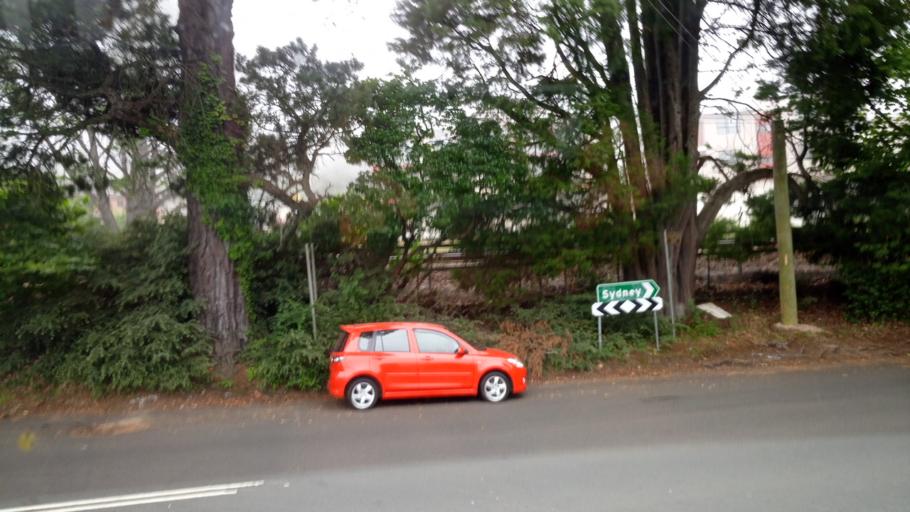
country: AU
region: New South Wales
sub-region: Blue Mountains Municipality
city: Leura
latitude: -33.7122
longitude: 150.3332
